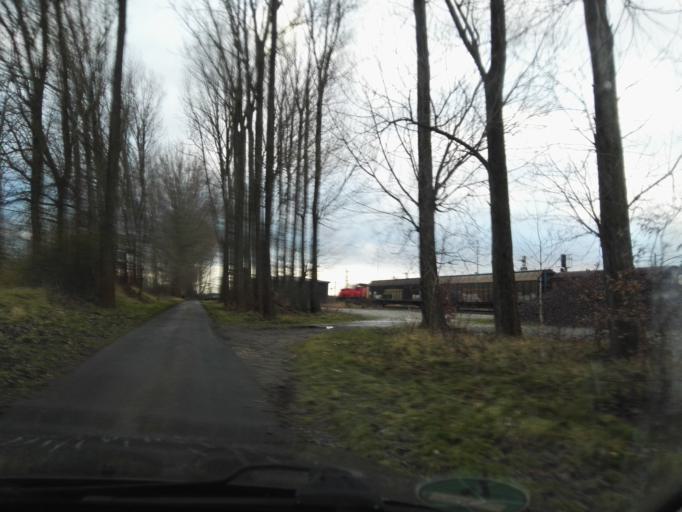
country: DE
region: Lower Saxony
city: Leiferde
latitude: 52.2190
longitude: 10.4511
